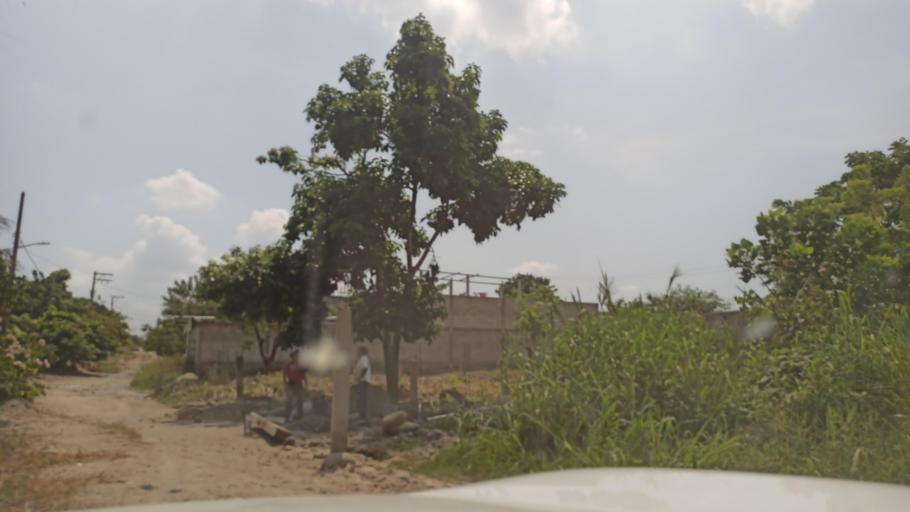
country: MX
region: Veracruz
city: Martinez de la Torre
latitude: 20.0789
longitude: -97.0762
